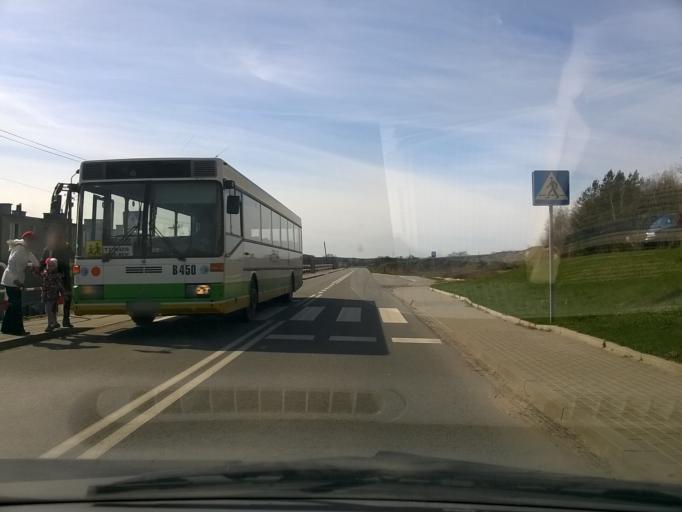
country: PL
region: Greater Poland Voivodeship
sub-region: Powiat wagrowiecki
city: Golancz
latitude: 53.0184
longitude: 17.3750
